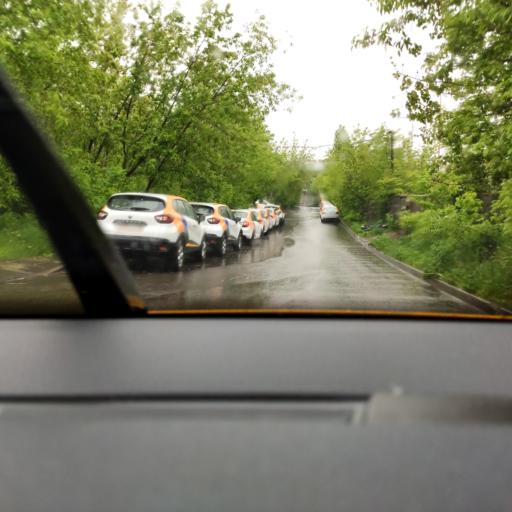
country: RU
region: Moscow
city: Strogino
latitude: 55.8405
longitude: 37.4273
